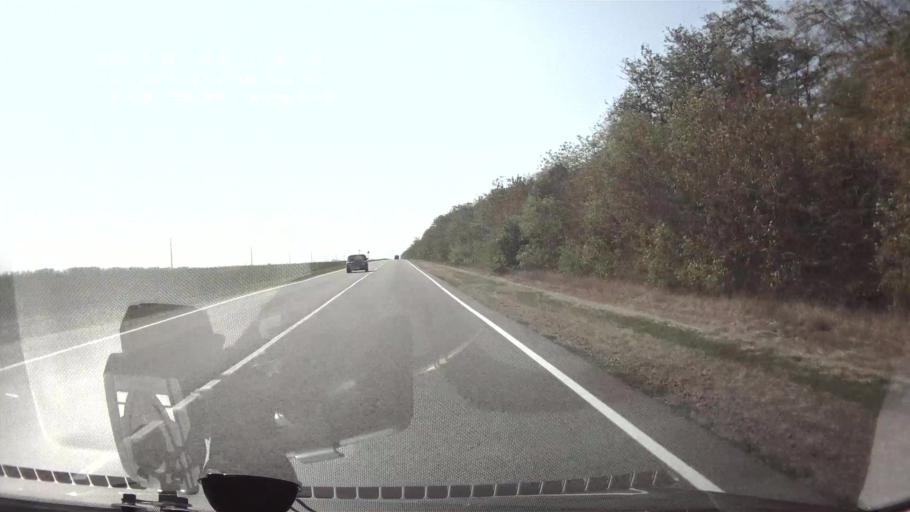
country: RU
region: Krasnodarskiy
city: Novopokrovskaya
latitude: 45.8760
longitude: 40.7205
